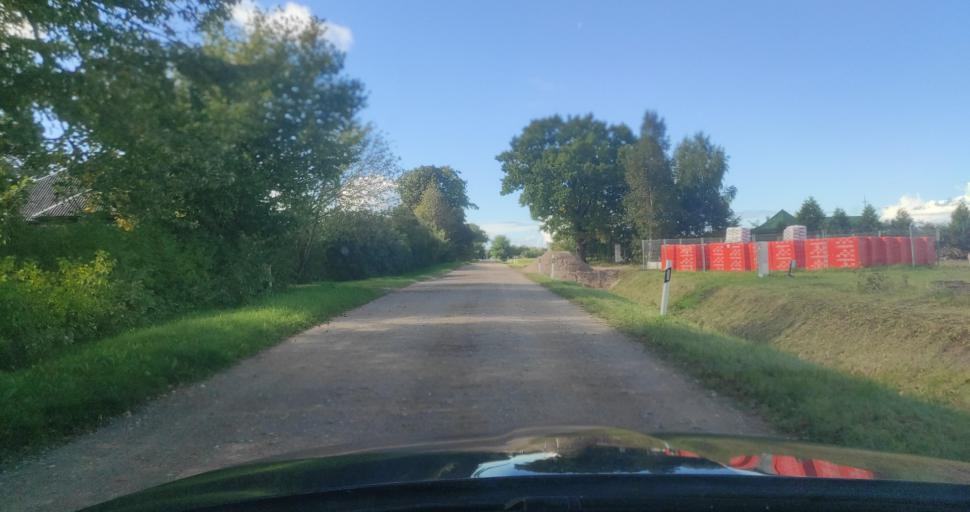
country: LV
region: Ventspils
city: Ventspils
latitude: 57.3656
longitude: 21.6114
